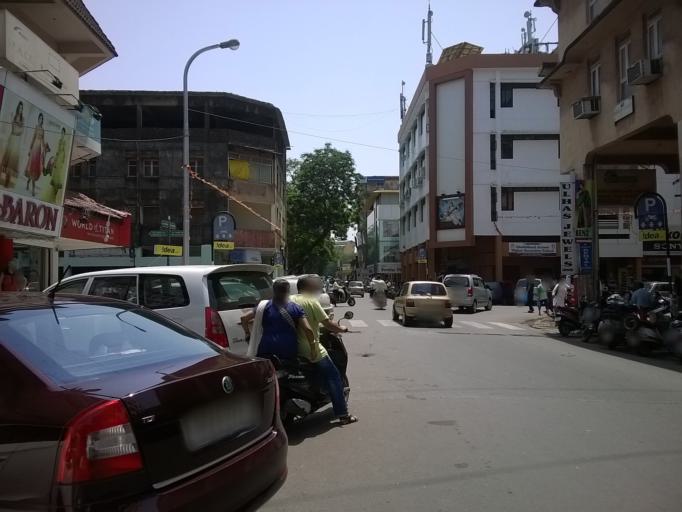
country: IN
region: Goa
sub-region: North Goa
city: Panaji
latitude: 15.4975
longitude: 73.8256
